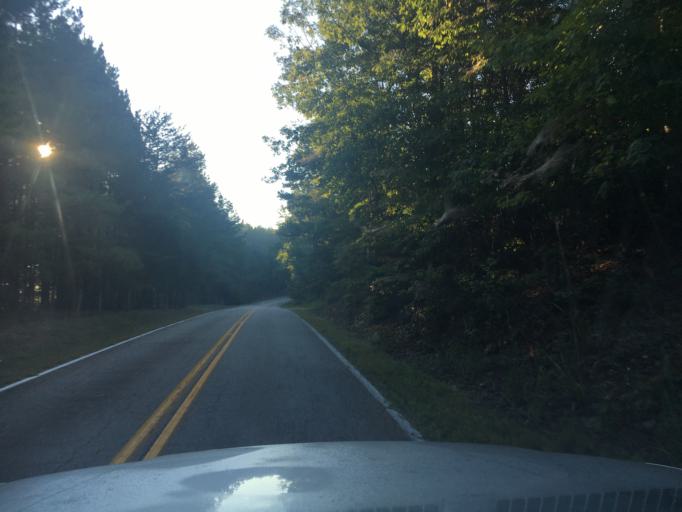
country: US
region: South Carolina
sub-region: Spartanburg County
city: Woodruff
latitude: 34.7848
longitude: -81.9901
